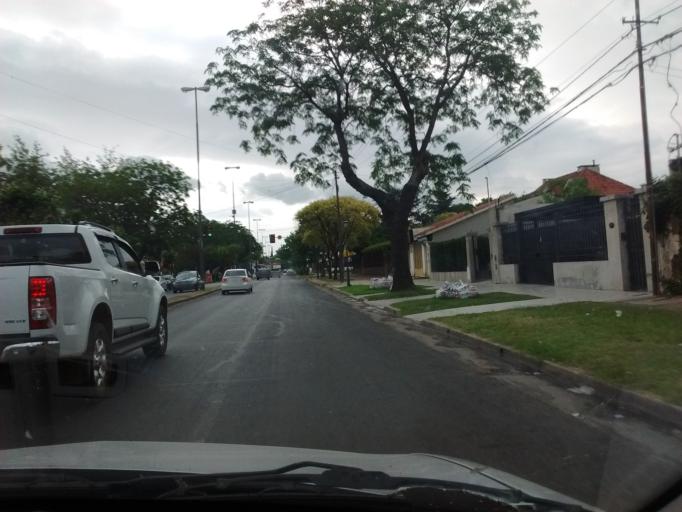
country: AR
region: Santa Fe
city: Granadero Baigorria
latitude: -32.9289
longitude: -60.7360
